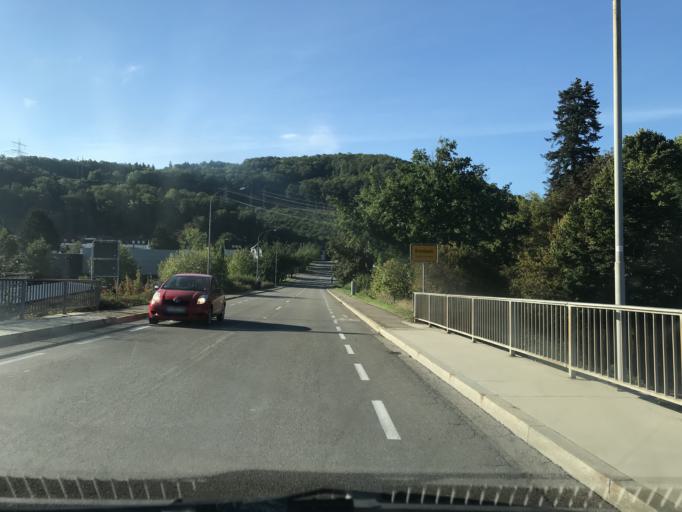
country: DE
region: Baden-Wuerttemberg
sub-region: Freiburg Region
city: Loerrach
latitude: 47.6328
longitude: 7.6821
